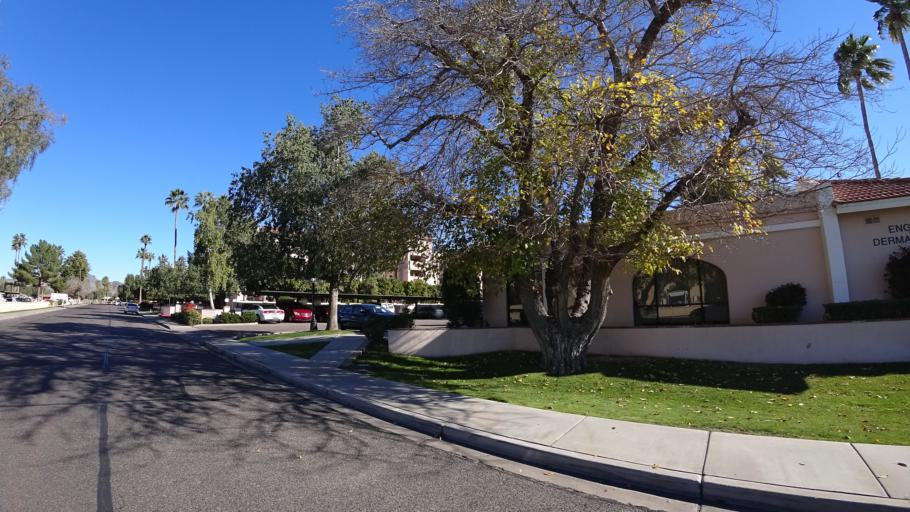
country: US
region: Arizona
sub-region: Maricopa County
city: Phoenix
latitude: 33.4953
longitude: -112.0162
